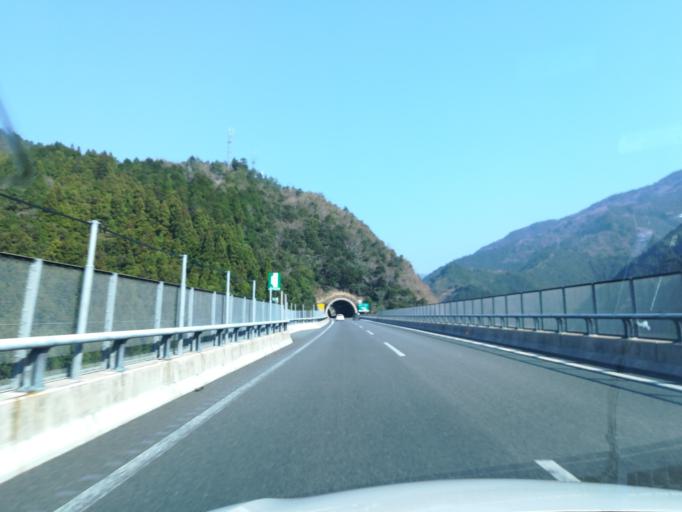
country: JP
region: Ehime
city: Kawanoecho
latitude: 33.8242
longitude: 133.6621
